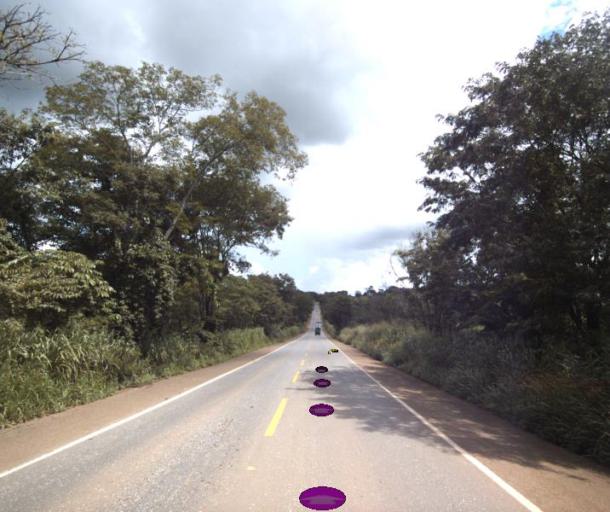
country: BR
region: Goias
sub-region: Pirenopolis
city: Pirenopolis
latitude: -16.0810
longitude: -49.0458
